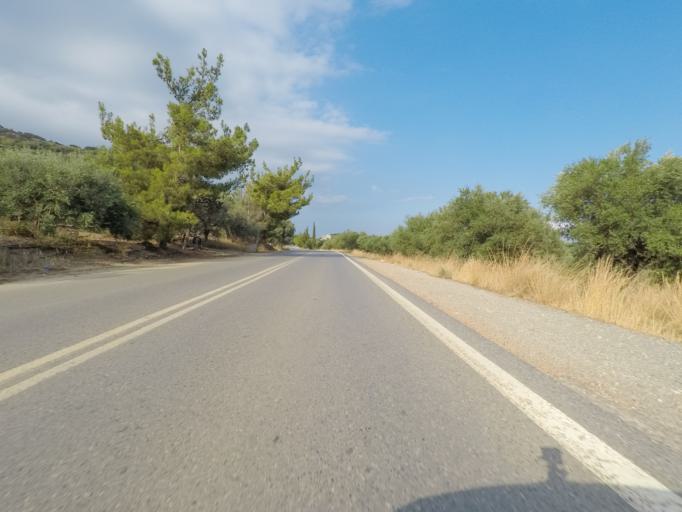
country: GR
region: Crete
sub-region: Nomos Lasithiou
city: Kritsa
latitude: 35.1564
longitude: 25.6811
